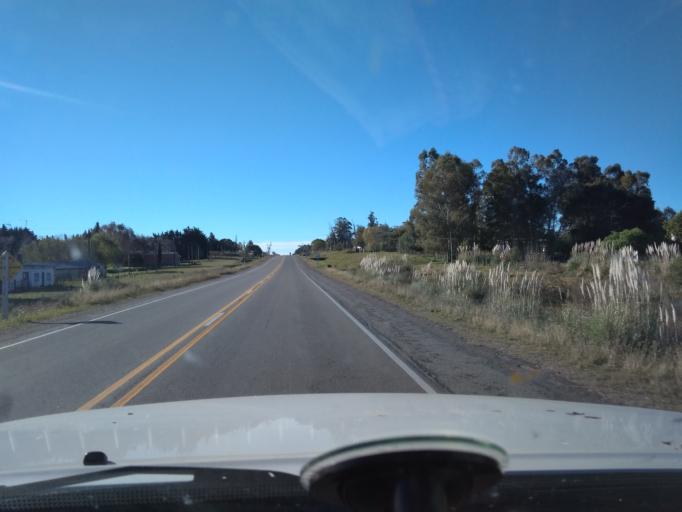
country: UY
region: Canelones
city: Sauce
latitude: -34.6148
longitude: -56.0491
